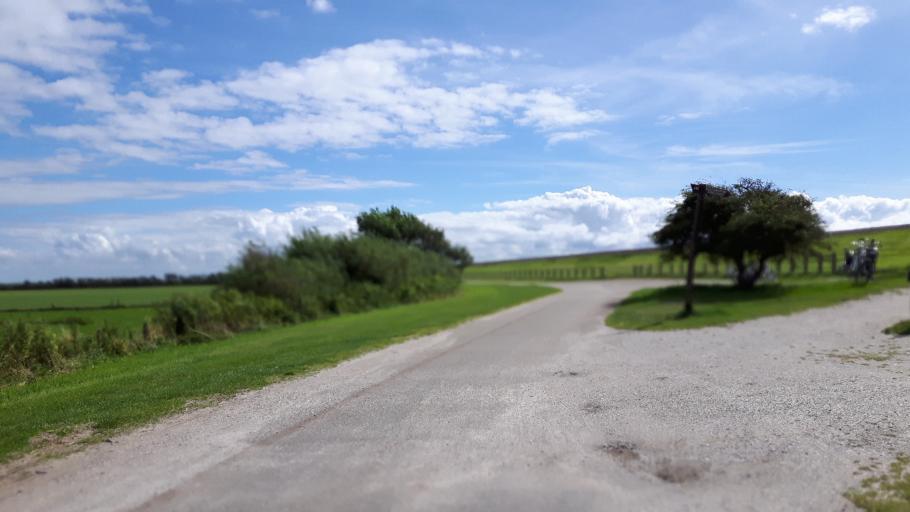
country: NL
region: Friesland
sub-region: Gemeente Ameland
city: Hollum
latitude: 53.4360
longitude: 5.6258
